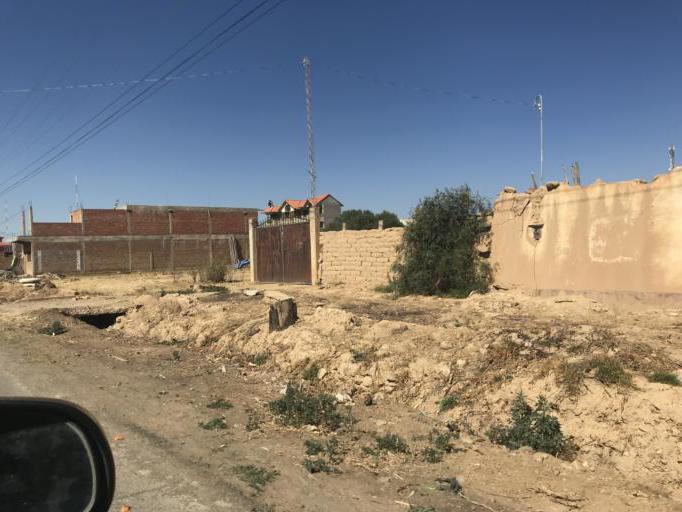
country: BO
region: Cochabamba
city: Cliza
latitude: -17.5947
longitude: -65.9461
